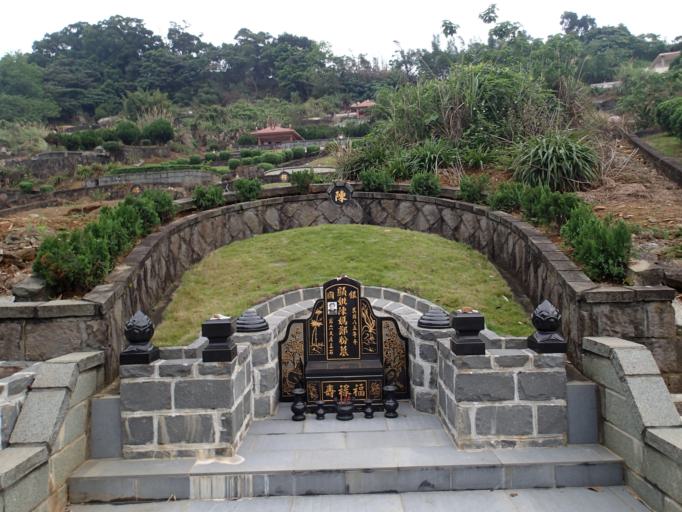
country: TW
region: Taipei
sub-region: Taipei
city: Banqiao
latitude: 25.1095
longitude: 121.4393
